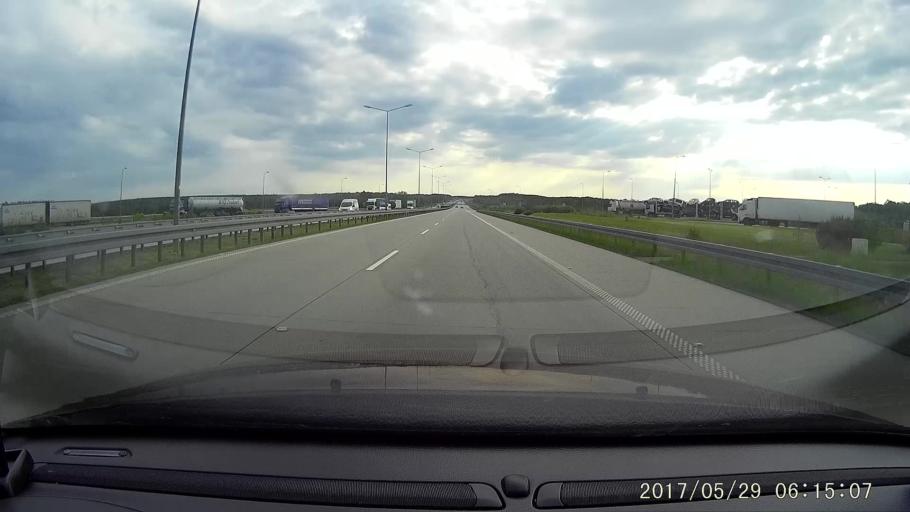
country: PL
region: Lower Silesian Voivodeship
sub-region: Powiat boleslawiecki
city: Nowogrodziec
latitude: 51.2479
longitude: 15.3454
